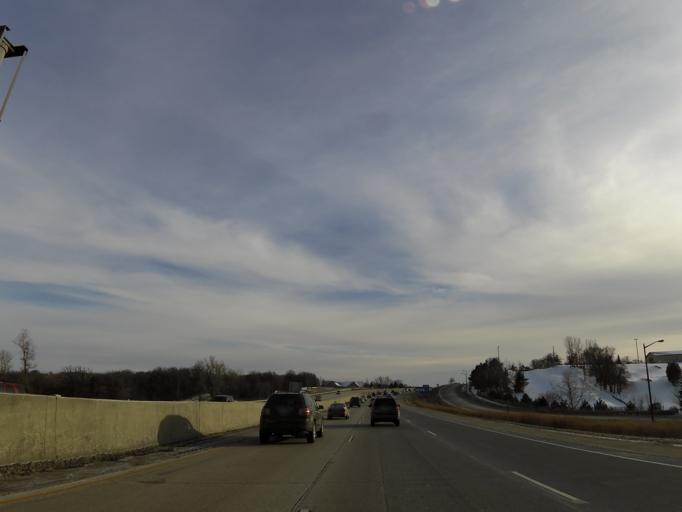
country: US
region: Minnesota
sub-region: Dakota County
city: Burnsville
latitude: 44.7244
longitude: -93.2821
